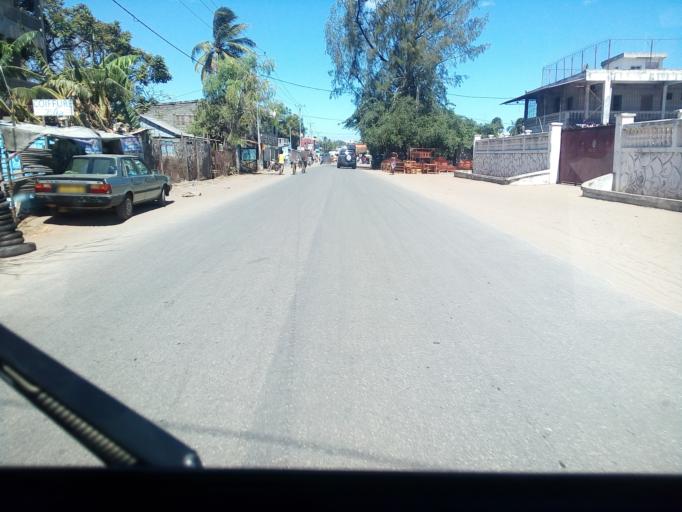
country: MG
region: Boeny
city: Mahajanga
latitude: -15.7040
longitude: 46.3225
